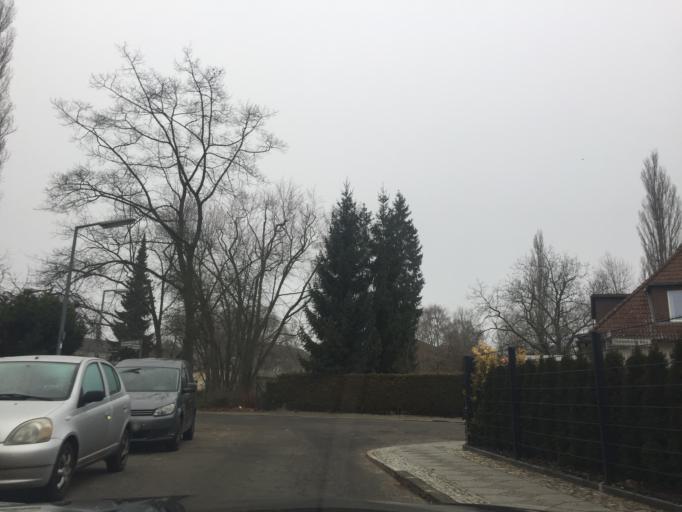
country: DE
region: Berlin
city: Tegel
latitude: 52.5885
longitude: 13.2978
